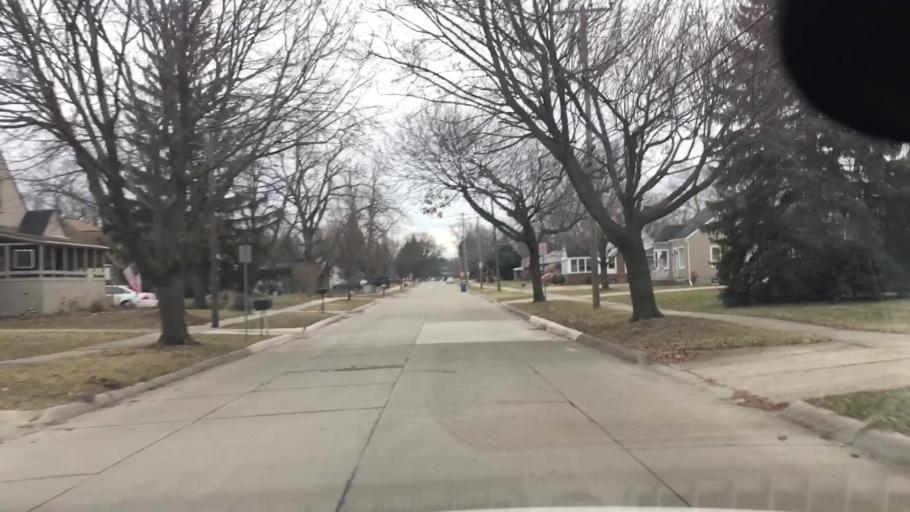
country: US
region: Michigan
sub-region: Oakland County
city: Madison Heights
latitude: 42.5035
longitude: -83.0738
